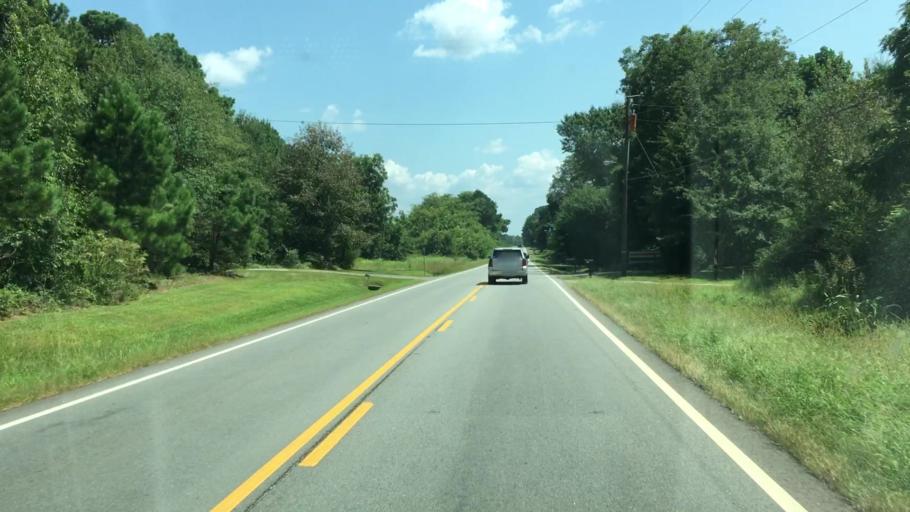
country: US
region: Georgia
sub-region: Oconee County
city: Watkinsville
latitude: 33.8139
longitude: -83.4346
